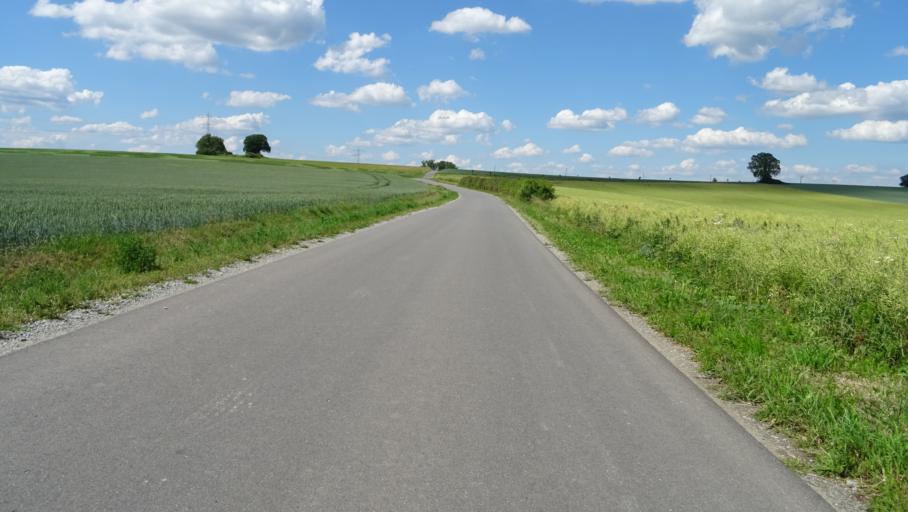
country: DE
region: Baden-Wuerttemberg
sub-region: Karlsruhe Region
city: Adelsheim
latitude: 49.3935
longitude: 9.3695
